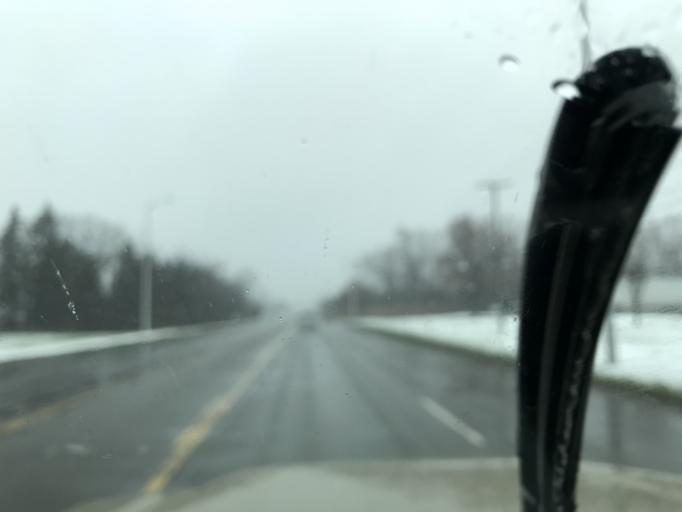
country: US
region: Michigan
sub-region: Wayne County
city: Woodhaven
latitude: 42.1734
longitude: -83.2273
